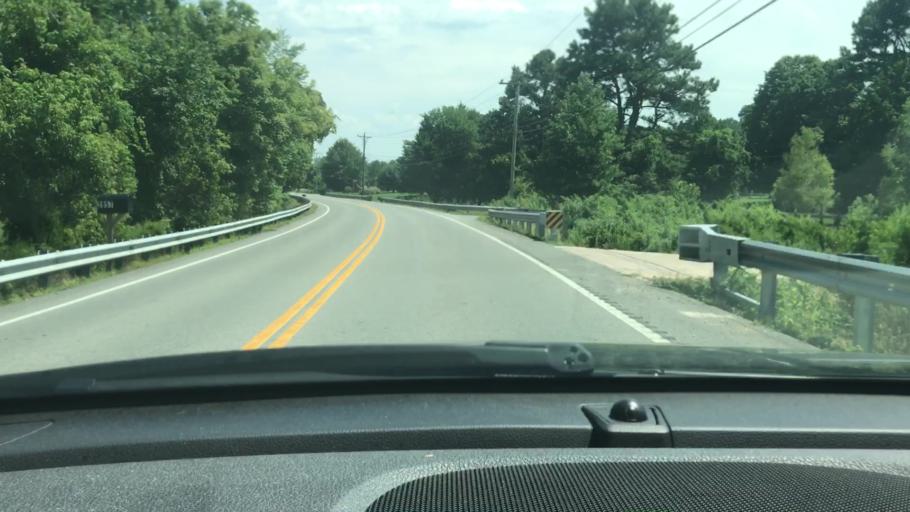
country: US
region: Tennessee
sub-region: Sumner County
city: Shackle Island
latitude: 36.4058
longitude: -86.6338
